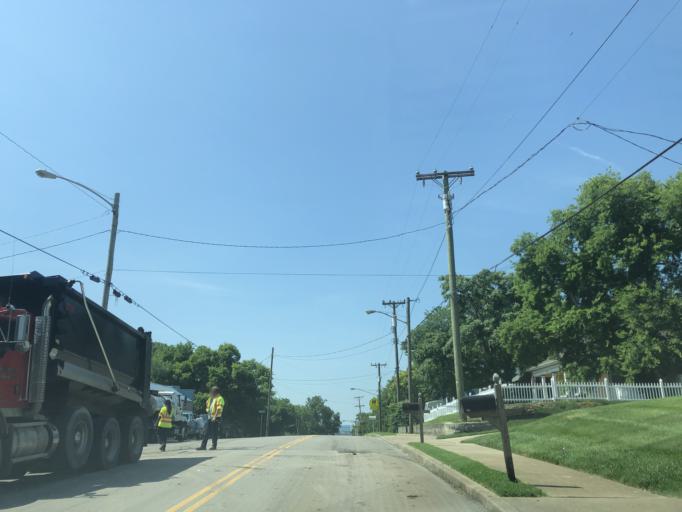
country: US
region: Tennessee
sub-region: Davidson County
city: Nashville
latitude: 36.2013
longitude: -86.7664
